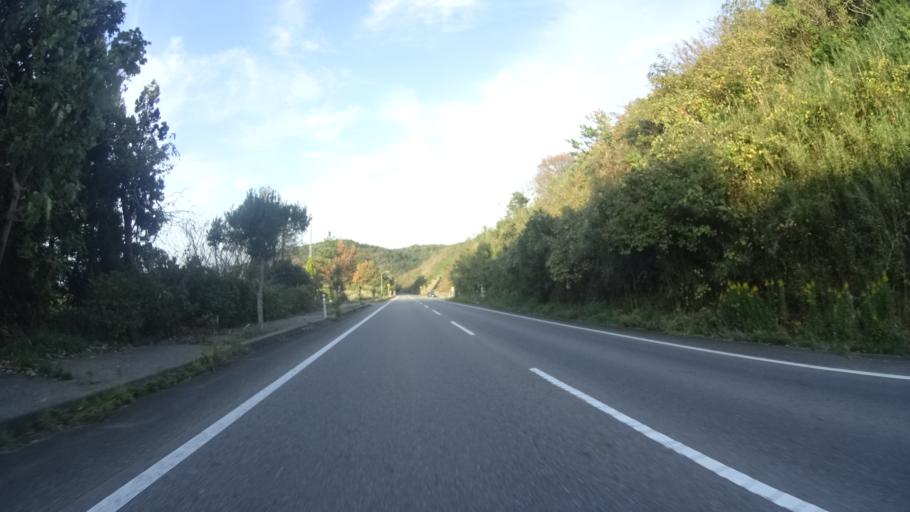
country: JP
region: Ishikawa
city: Hakui
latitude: 37.1144
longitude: 136.7280
